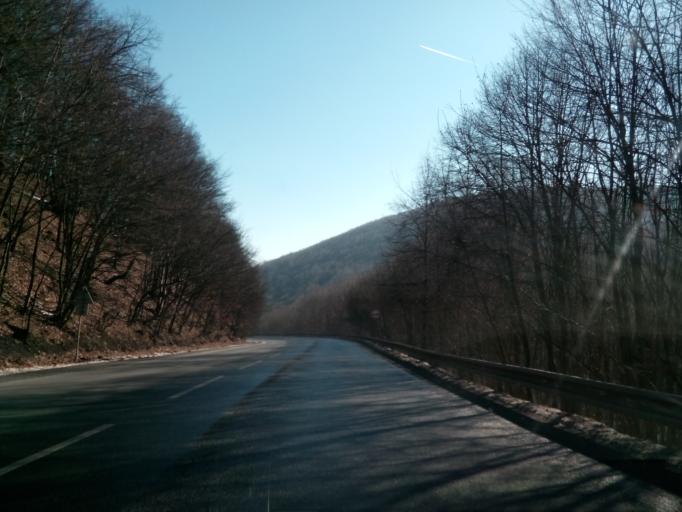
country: SK
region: Kosicky
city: Secovce
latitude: 48.7350
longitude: 21.5478
